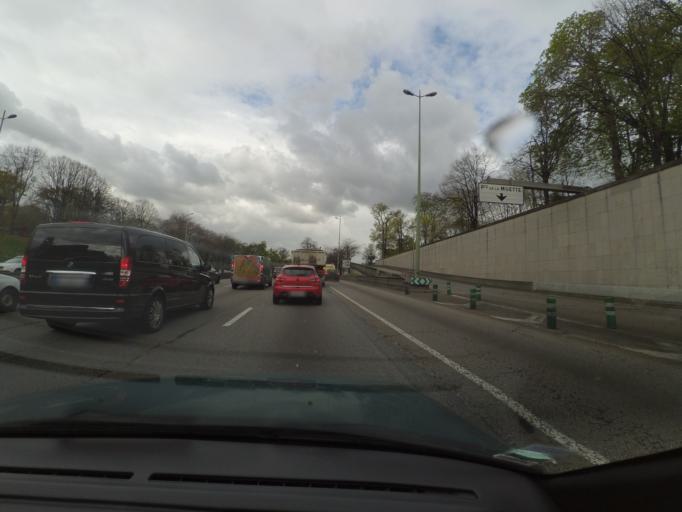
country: FR
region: Ile-de-France
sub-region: Departement des Hauts-de-Seine
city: Neuilly-sur-Seine
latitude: 48.8611
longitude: 2.2641
